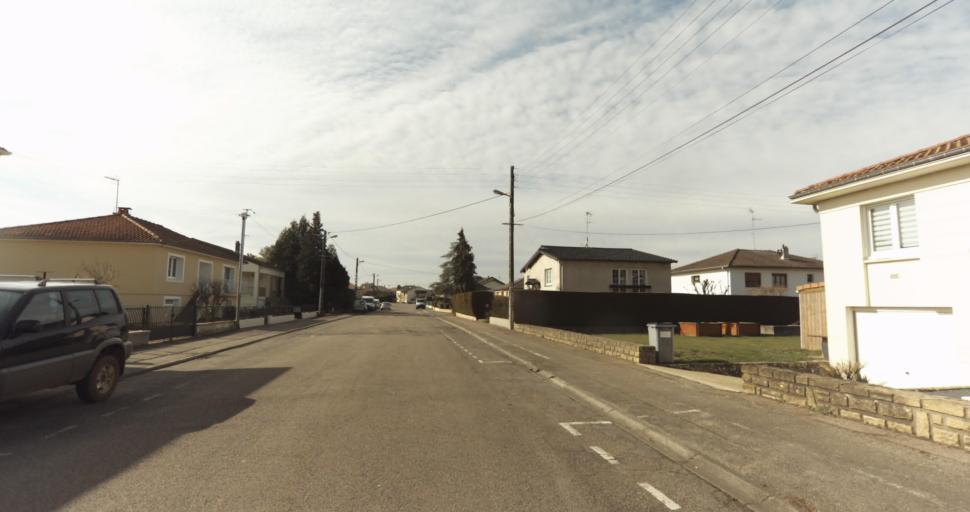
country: FR
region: Lorraine
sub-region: Departement de Meurthe-et-Moselle
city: Jarny
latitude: 49.1537
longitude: 5.8754
